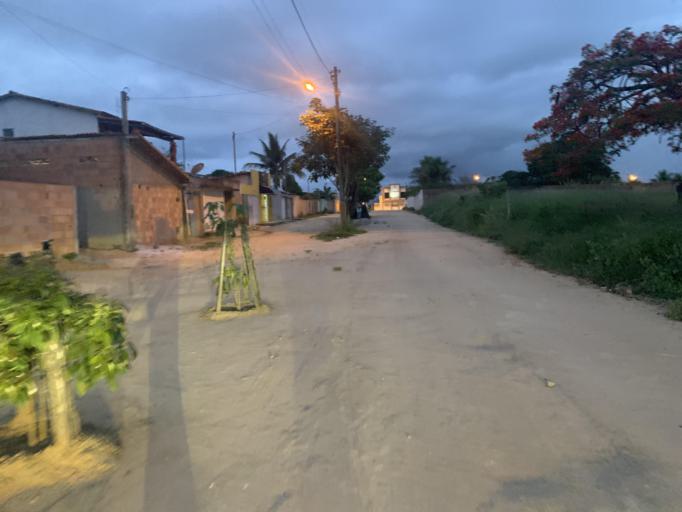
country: BR
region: Bahia
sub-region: Medeiros Neto
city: Medeiros Neto
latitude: -17.3894
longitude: -40.2342
